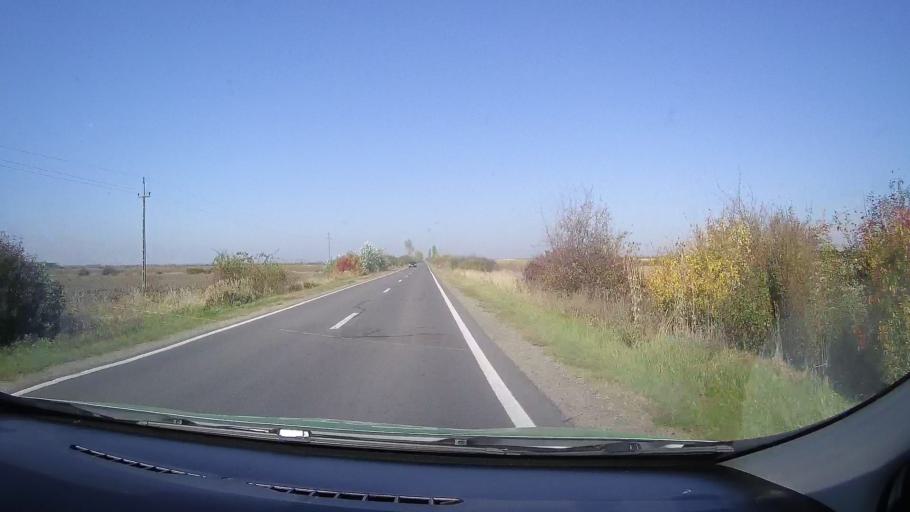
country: RO
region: Satu Mare
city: Carei
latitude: 47.7050
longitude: 22.4336
